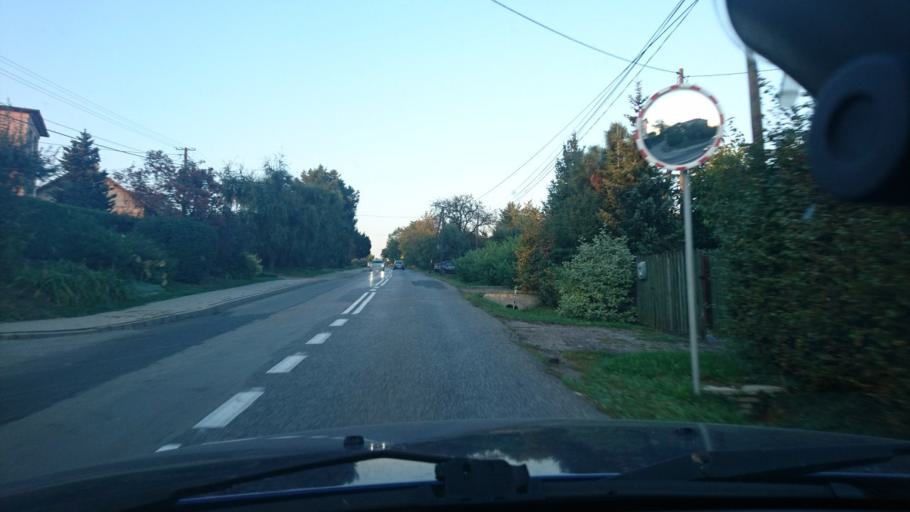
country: PL
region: Silesian Voivodeship
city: Janowice
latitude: 49.9021
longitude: 19.0814
